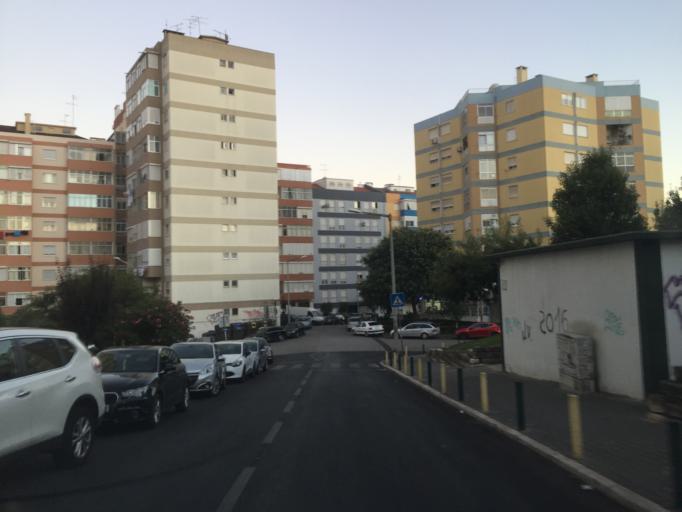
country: PT
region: Lisbon
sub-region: Odivelas
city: Povoa de Santo Adriao
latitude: 38.7967
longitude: -9.1652
